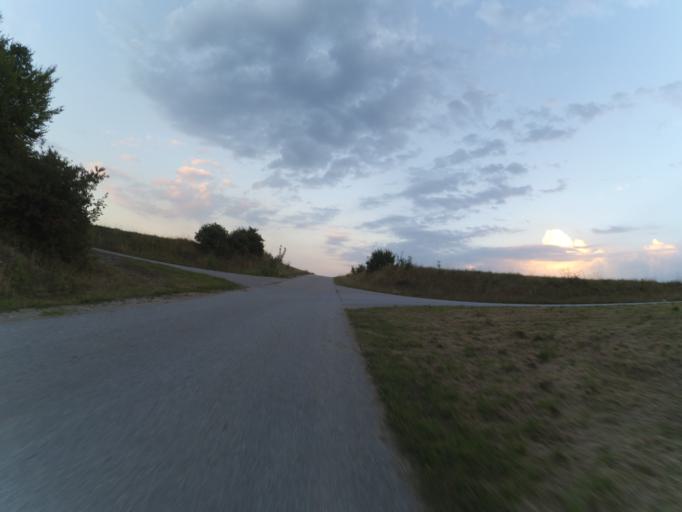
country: DE
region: Bavaria
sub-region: Swabia
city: Turkheim
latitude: 48.0558
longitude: 10.5944
